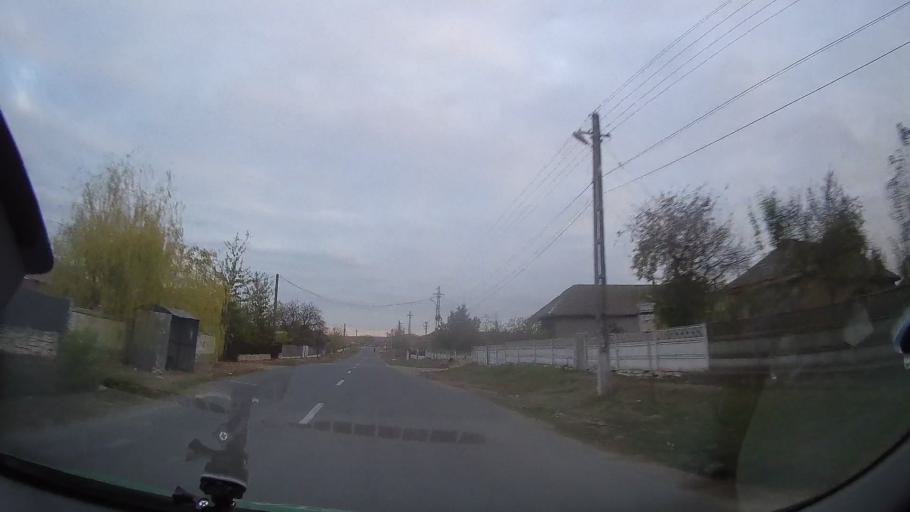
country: RO
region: Tulcea
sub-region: Comuna Mihai Bravu
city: Turda
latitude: 44.9749
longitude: 28.6227
